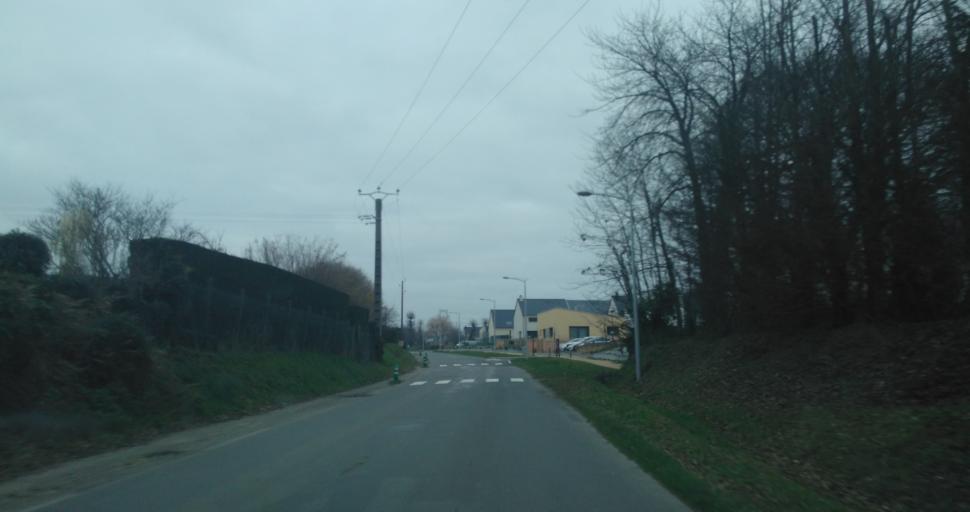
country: FR
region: Brittany
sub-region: Departement d'Ille-et-Vilaine
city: Romille
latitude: 48.2200
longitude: -1.8920
